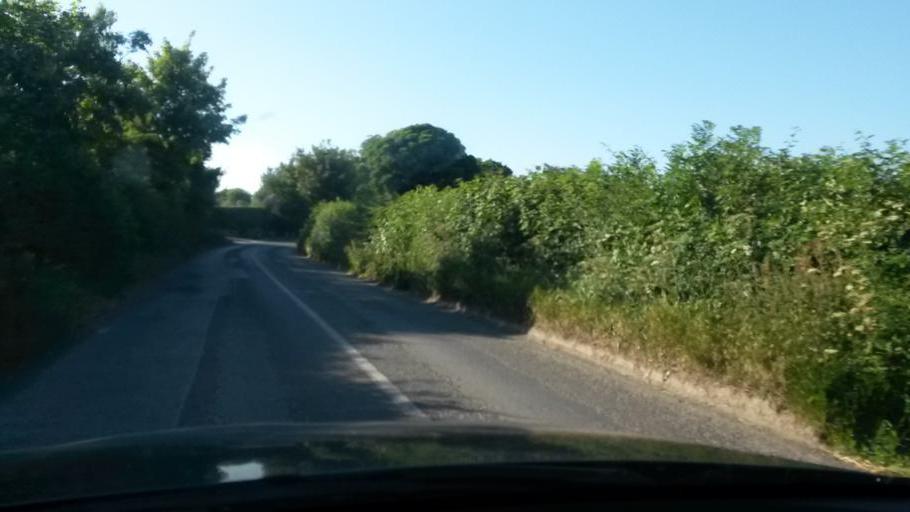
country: IE
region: Leinster
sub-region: Dublin City
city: Finglas
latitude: 53.4573
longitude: -6.3105
